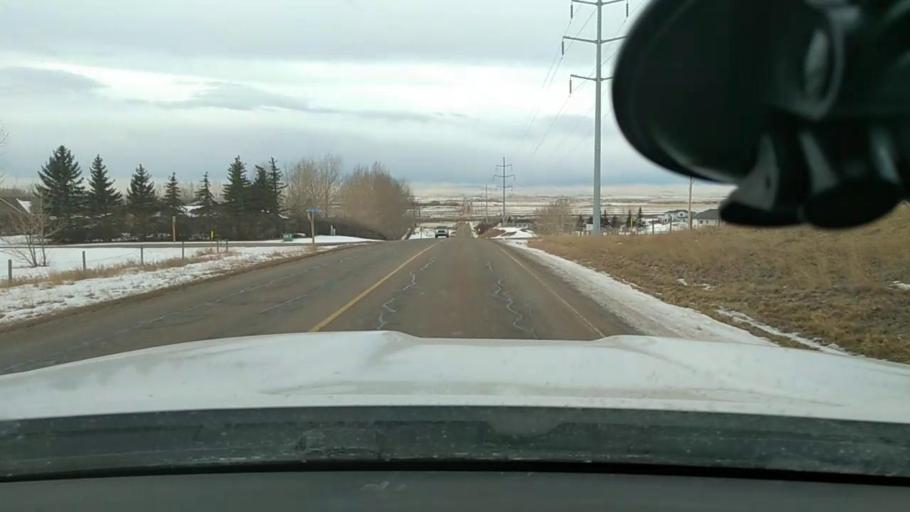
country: CA
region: Alberta
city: Airdrie
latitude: 51.2417
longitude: -113.9866
